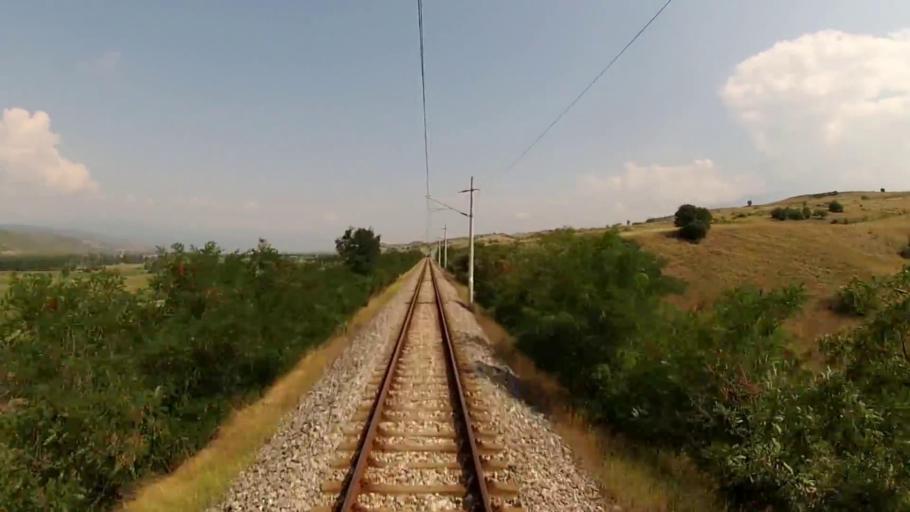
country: BG
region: Blagoevgrad
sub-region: Obshtina Sandanski
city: Sandanski
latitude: 41.5843
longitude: 23.2383
